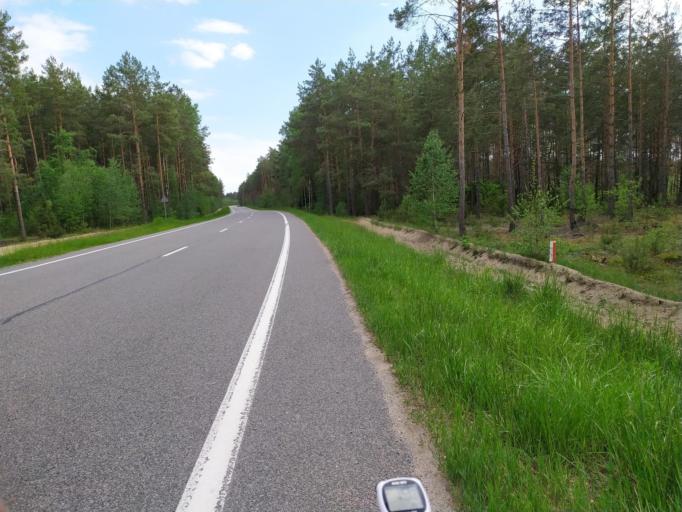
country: BY
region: Brest
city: Zhabinka
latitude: 52.4542
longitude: 24.1372
